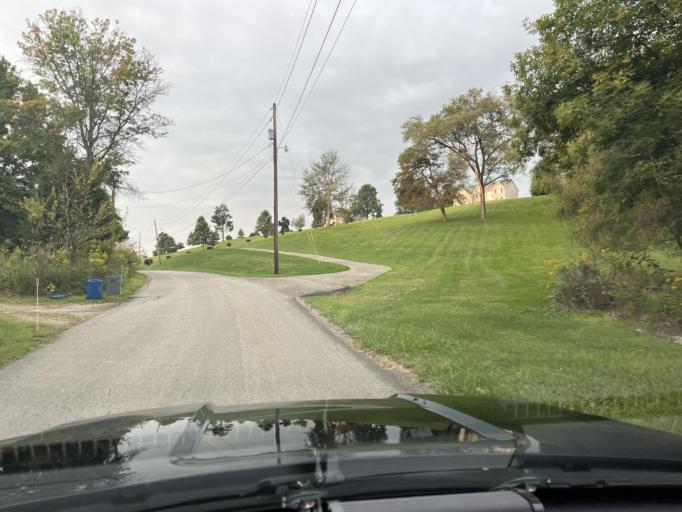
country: US
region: Pennsylvania
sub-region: Fayette County
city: South Uniontown
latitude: 39.8878
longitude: -79.7722
